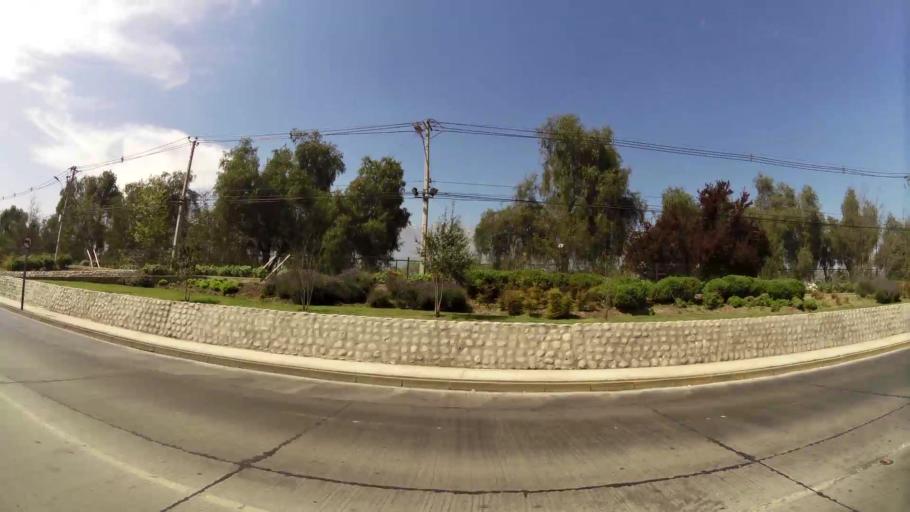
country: CL
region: Santiago Metropolitan
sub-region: Provincia de Santiago
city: Villa Presidente Frei, Nunoa, Santiago, Chile
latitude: -33.4725
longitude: -70.5546
